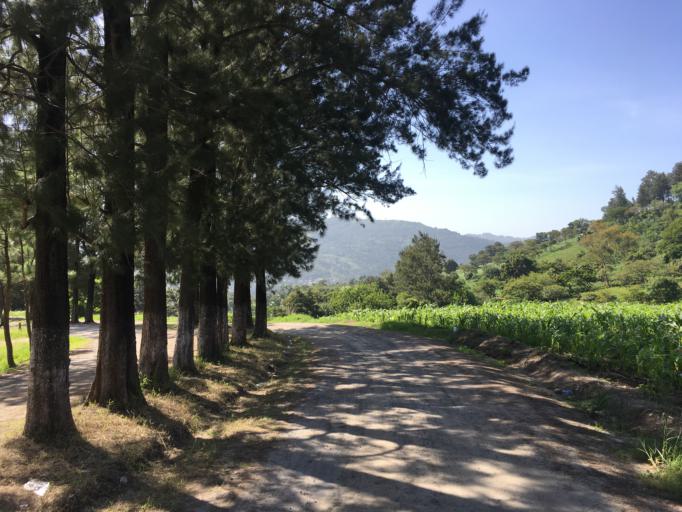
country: GT
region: Guatemala
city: Villa Canales
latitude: 14.4837
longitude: -90.5452
